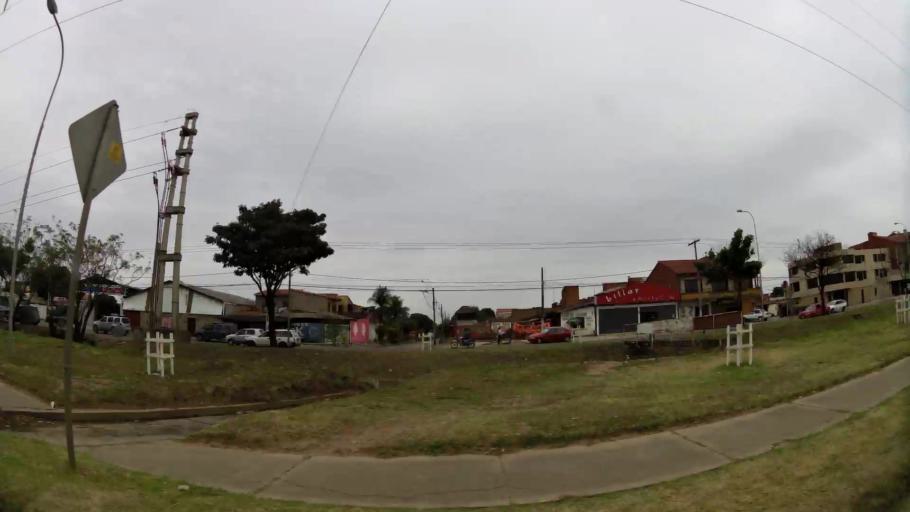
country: BO
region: Santa Cruz
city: Santa Cruz de la Sierra
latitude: -17.7576
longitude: -63.1505
